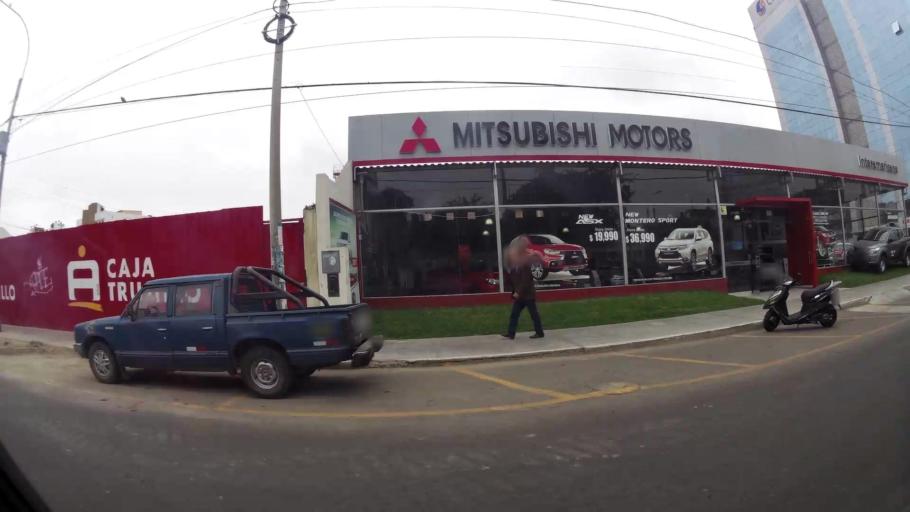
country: PE
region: La Libertad
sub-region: Provincia de Trujillo
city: Trujillo
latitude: -8.1225
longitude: -79.0345
